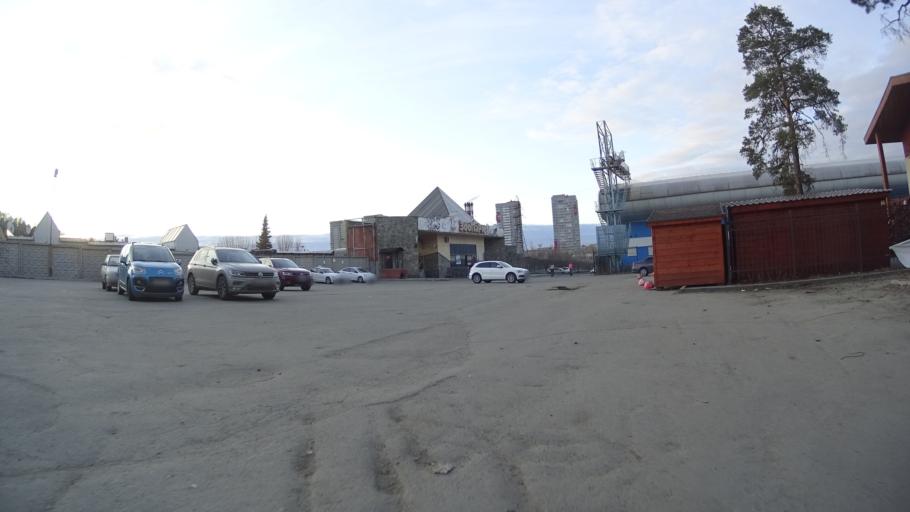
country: RU
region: Chelyabinsk
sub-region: Gorod Chelyabinsk
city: Chelyabinsk
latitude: 55.1675
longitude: 61.3701
